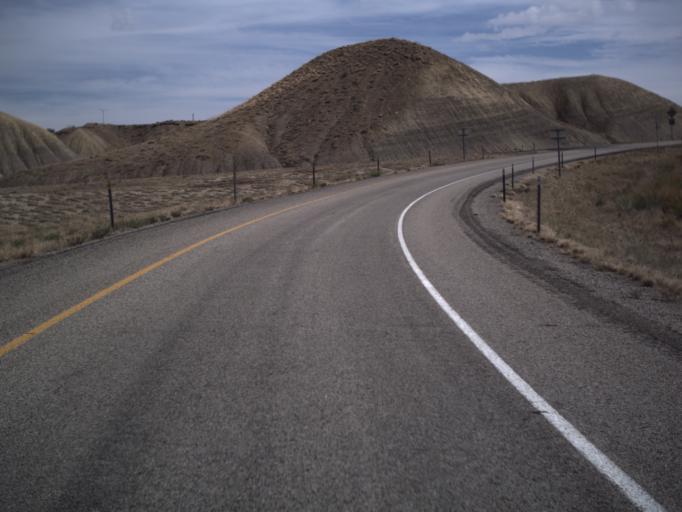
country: US
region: Utah
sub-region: Grand County
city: Moab
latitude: 38.9375
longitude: -109.8348
